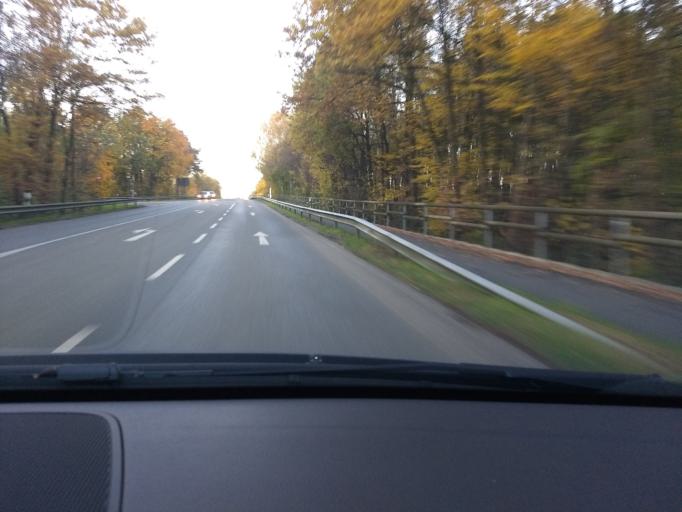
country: DE
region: North Rhine-Westphalia
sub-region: Regierungsbezirk Munster
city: Heiden
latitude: 51.8428
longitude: 6.9049
